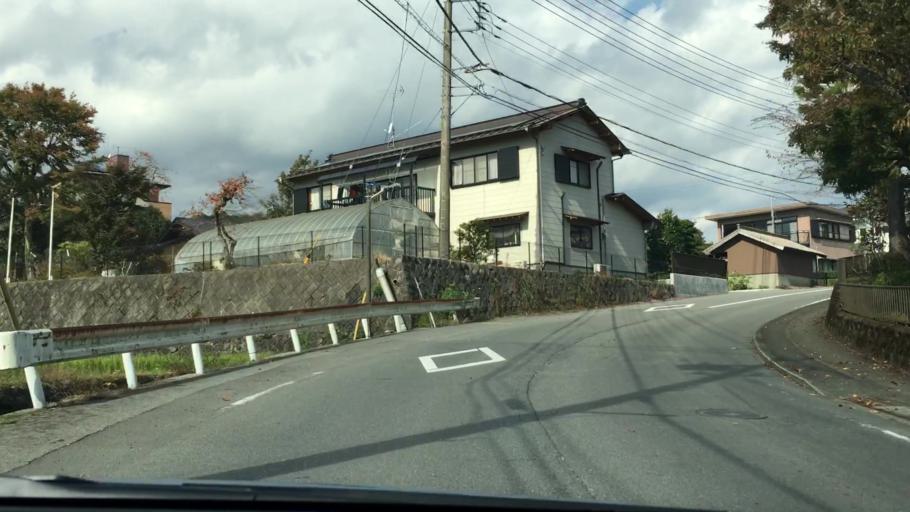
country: JP
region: Shizuoka
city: Gotemba
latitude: 35.3511
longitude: 138.9446
